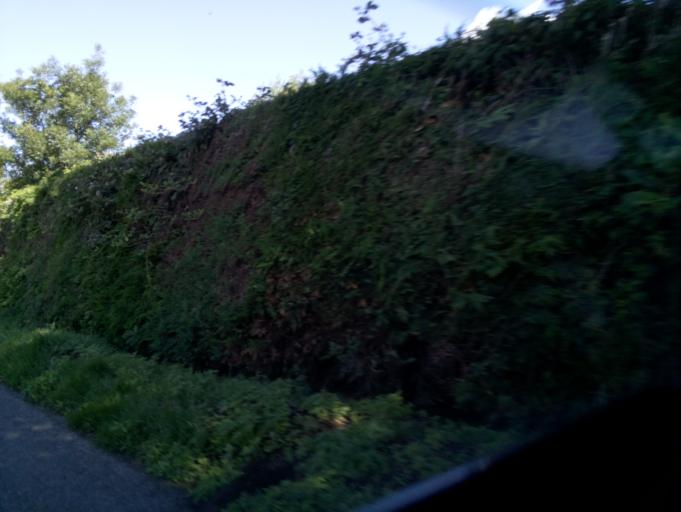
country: GB
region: England
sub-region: Herefordshire
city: Linton
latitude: 51.9398
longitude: -2.5220
